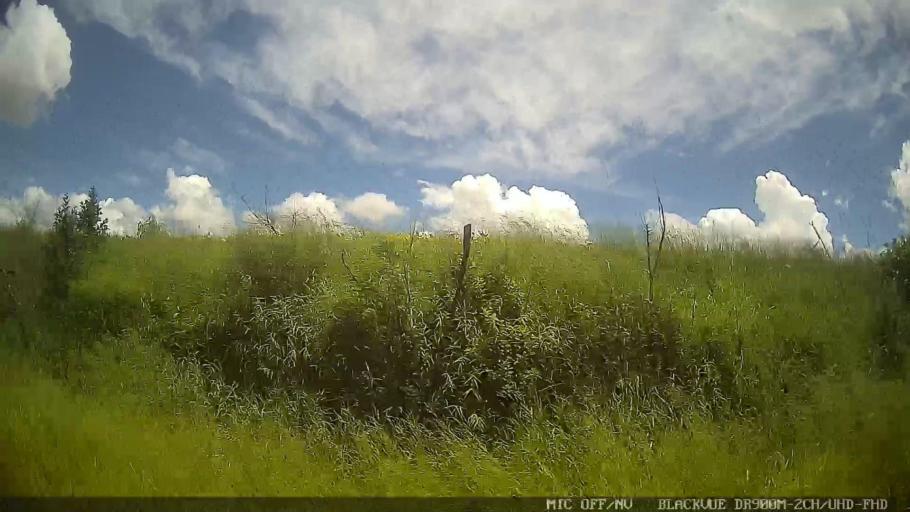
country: BR
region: Minas Gerais
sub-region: Extrema
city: Extrema
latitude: -22.7247
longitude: -46.4026
